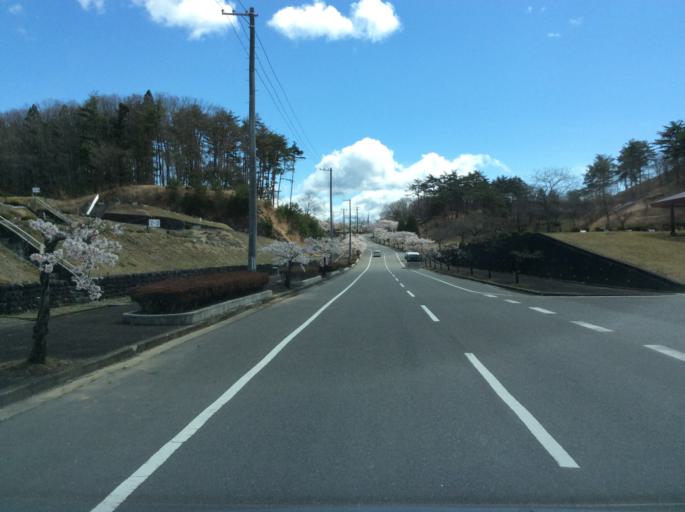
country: JP
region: Fukushima
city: Koriyama
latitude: 37.3485
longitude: 140.4332
